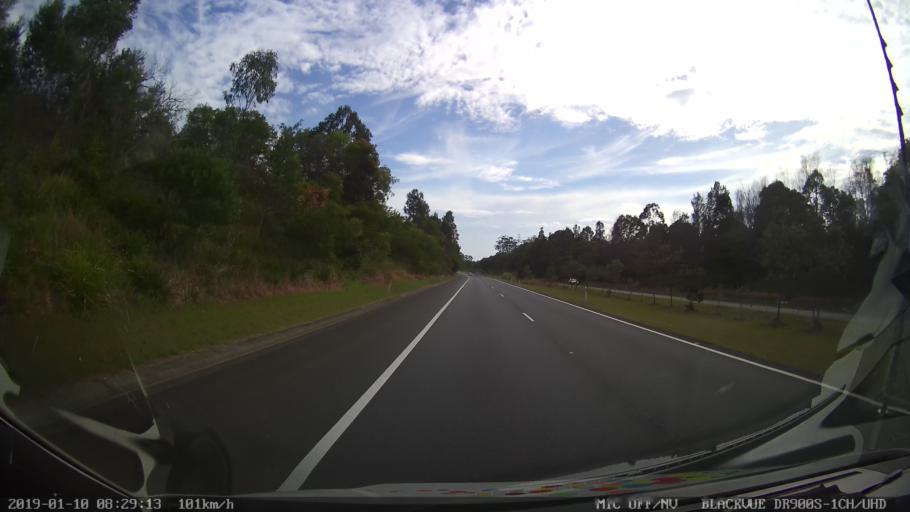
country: AU
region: New South Wales
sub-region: Coffs Harbour
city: Bonville
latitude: -30.3852
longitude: 153.0431
